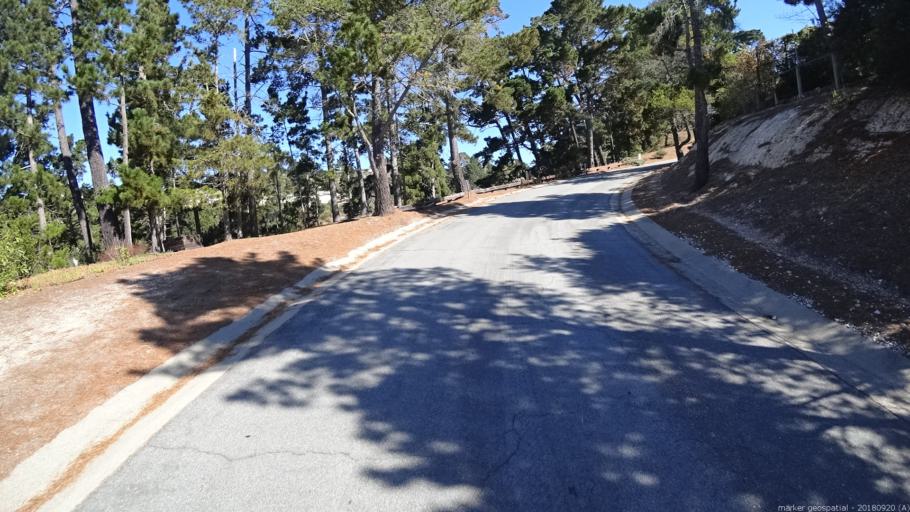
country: US
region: California
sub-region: Monterey County
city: Carmel-by-the-Sea
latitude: 36.5592
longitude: -121.8960
